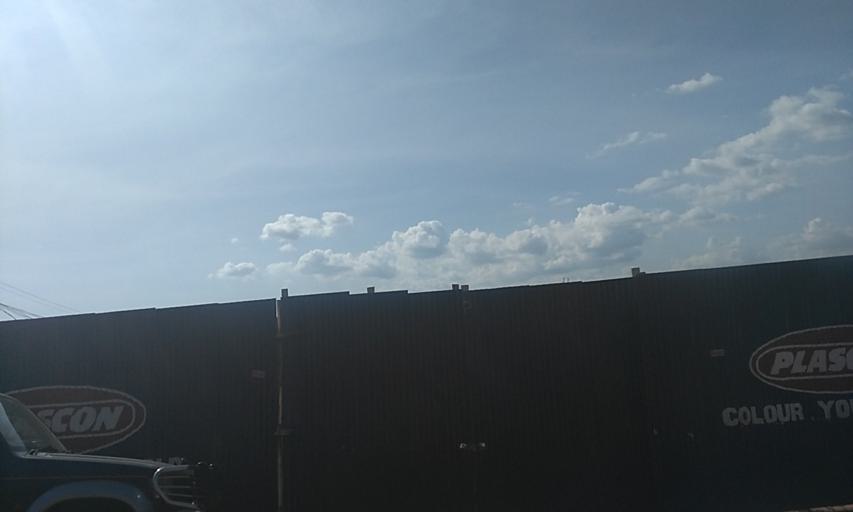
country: UG
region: Central Region
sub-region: Wakiso District
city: Kireka
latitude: 0.3671
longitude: 32.6247
